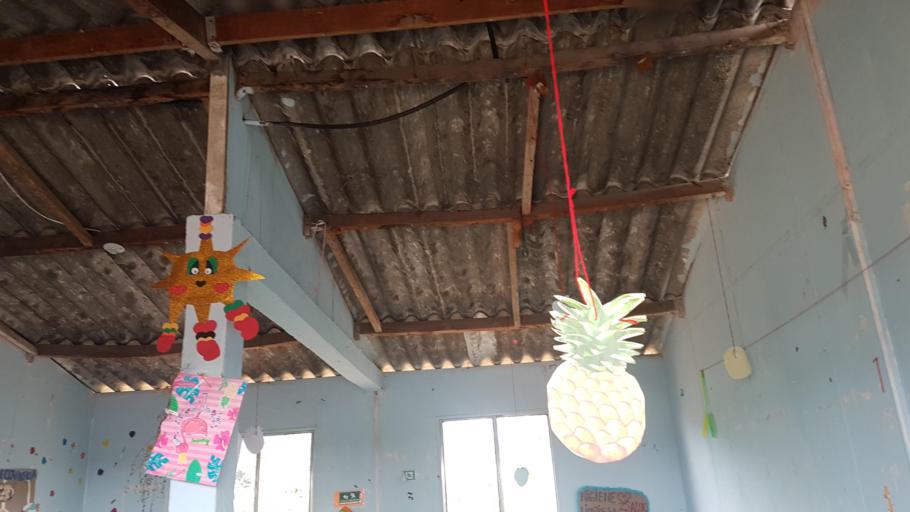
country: CO
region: Cauca
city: Buenos Aires
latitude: 3.1413
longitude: -76.6920
